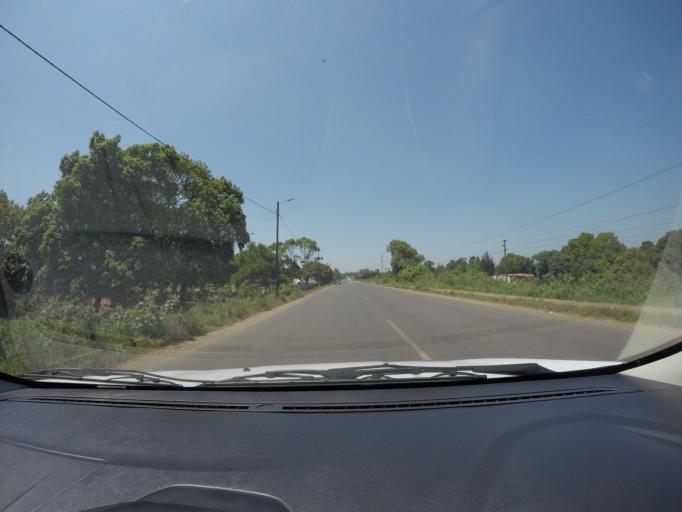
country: ZA
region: KwaZulu-Natal
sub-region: uThungulu District Municipality
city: eSikhawini
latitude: -28.8351
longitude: 31.9388
